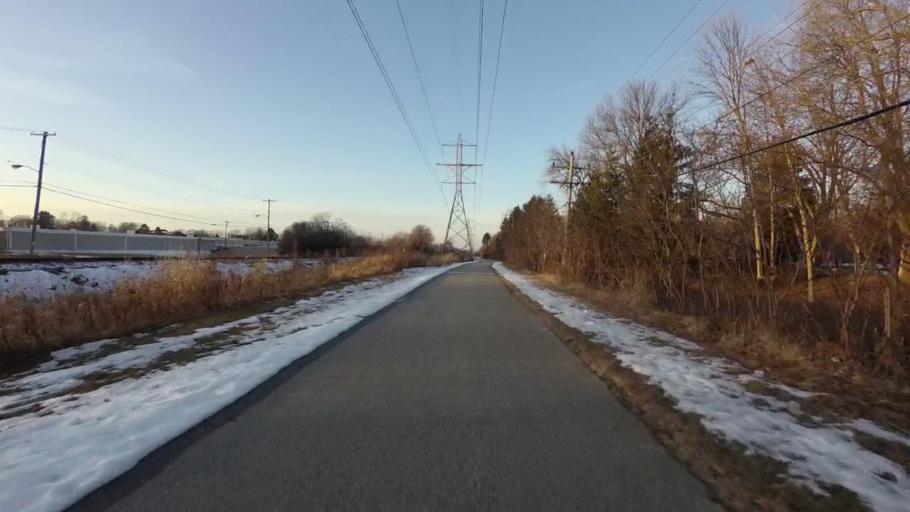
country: US
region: Wisconsin
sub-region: Milwaukee County
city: Brown Deer
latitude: 43.1635
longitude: -87.9609
